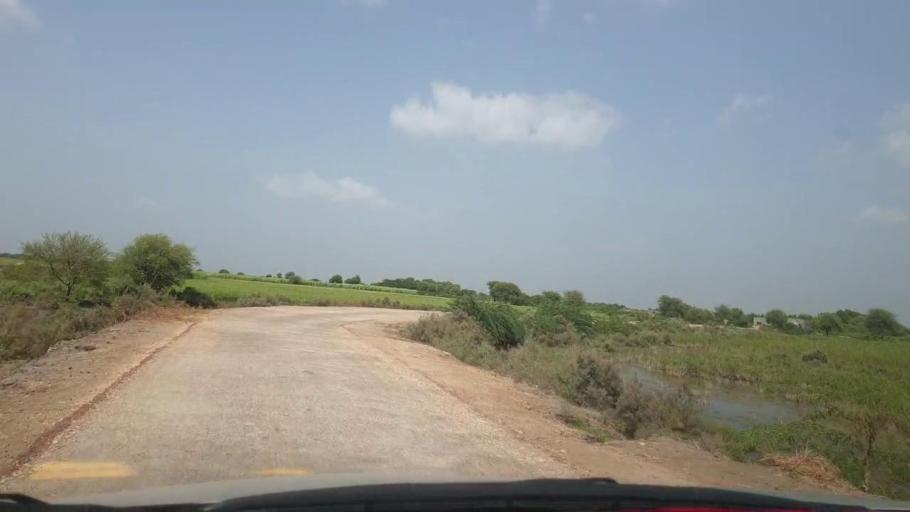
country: PK
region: Sindh
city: Tando Bago
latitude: 24.8723
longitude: 68.9274
